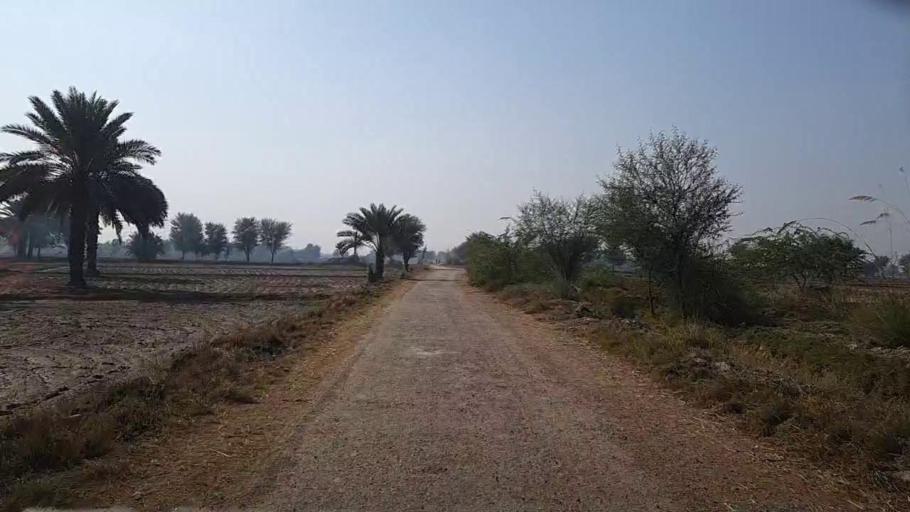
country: PK
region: Sindh
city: Bozdar
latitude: 27.2476
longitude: 68.6075
